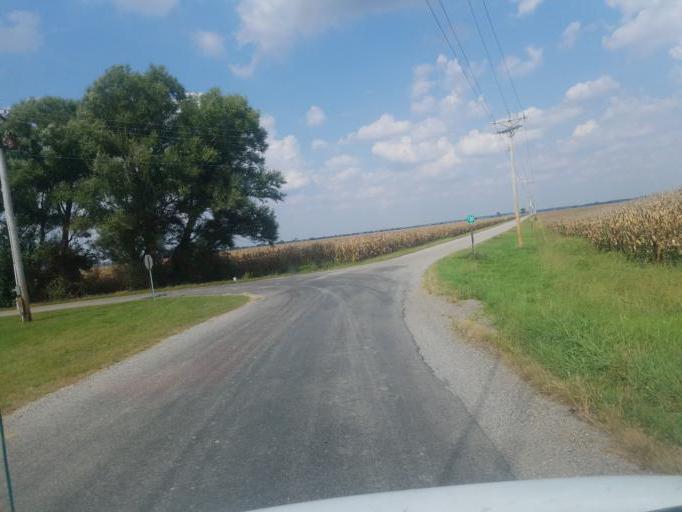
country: US
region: Ohio
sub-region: Hardin County
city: Ada
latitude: 40.6401
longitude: -83.7852
